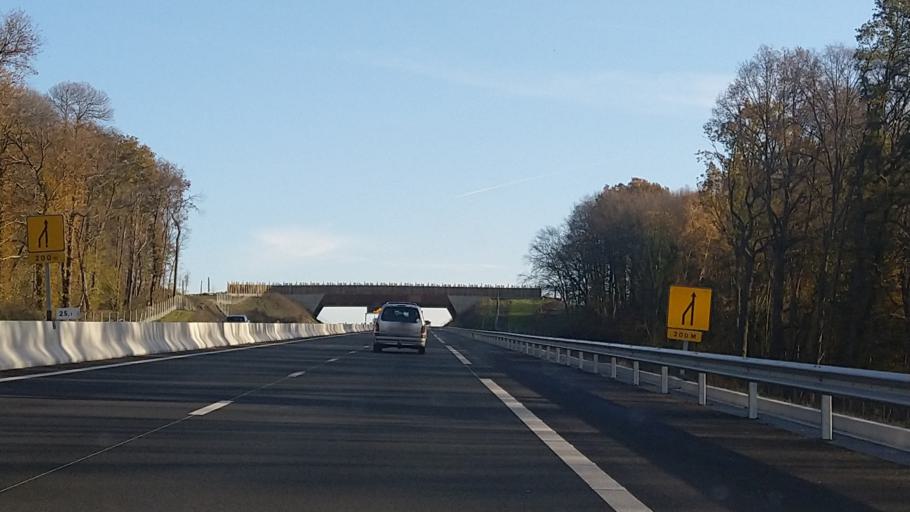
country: FR
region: Ile-de-France
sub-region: Departement du Val-d'Oise
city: Maffliers
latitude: 49.0926
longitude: 2.3034
